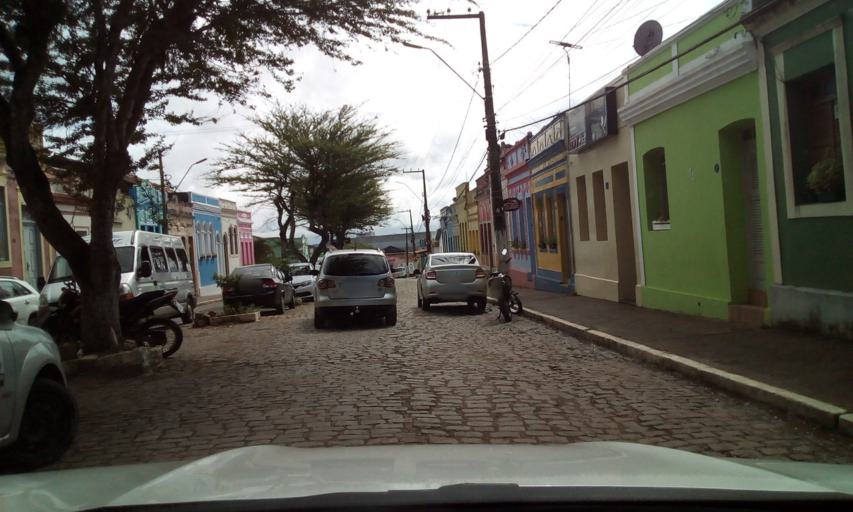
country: BR
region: Paraiba
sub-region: Areia
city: Areia
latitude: -6.9687
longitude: -35.7046
